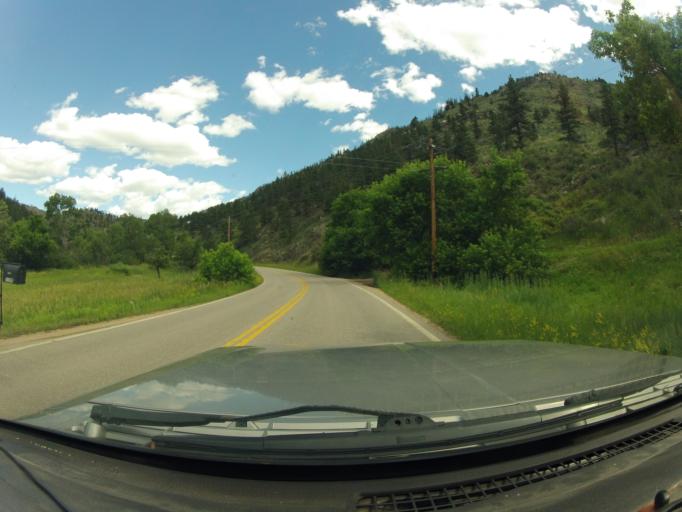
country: US
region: Colorado
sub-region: Larimer County
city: Laporte
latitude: 40.5728
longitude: -105.3233
